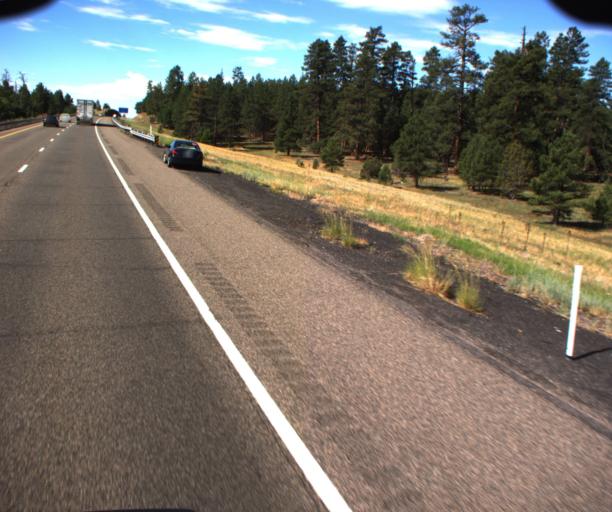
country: US
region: Arizona
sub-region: Coconino County
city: Sedona
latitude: 34.8313
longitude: -111.6071
